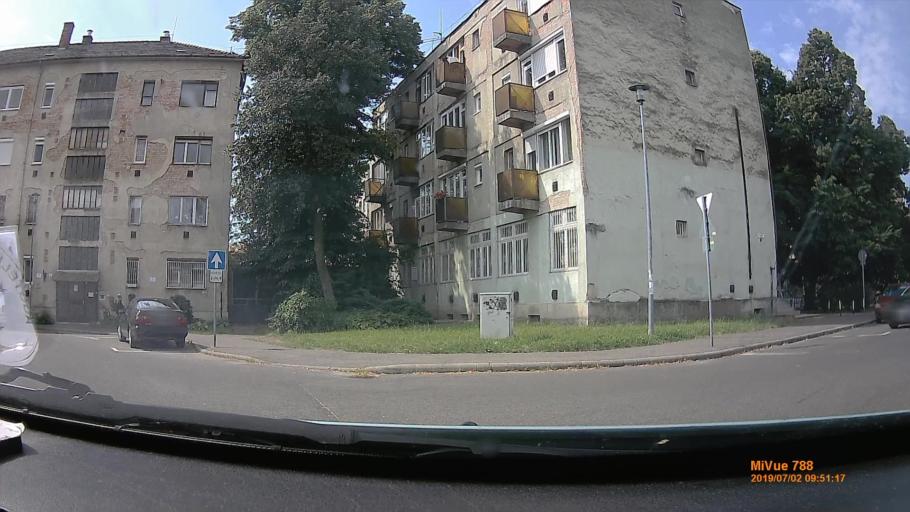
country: HU
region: Borsod-Abauj-Zemplen
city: Miskolc
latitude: 48.1038
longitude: 20.8042
